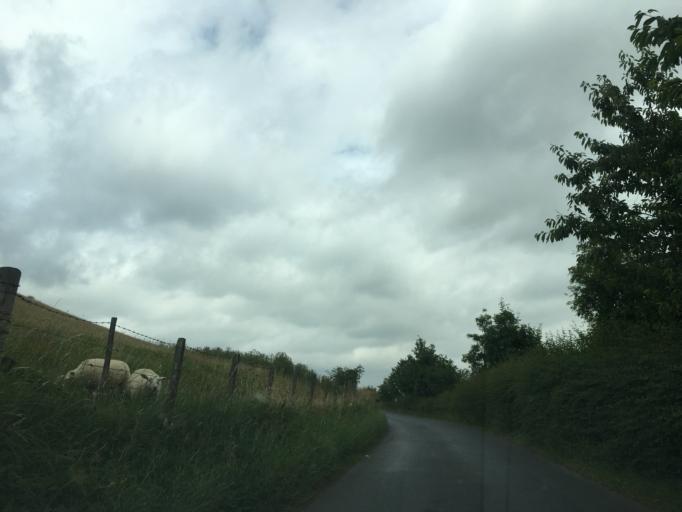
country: GB
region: Scotland
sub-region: The Scottish Borders
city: Peebles
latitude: 55.6675
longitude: -3.2035
